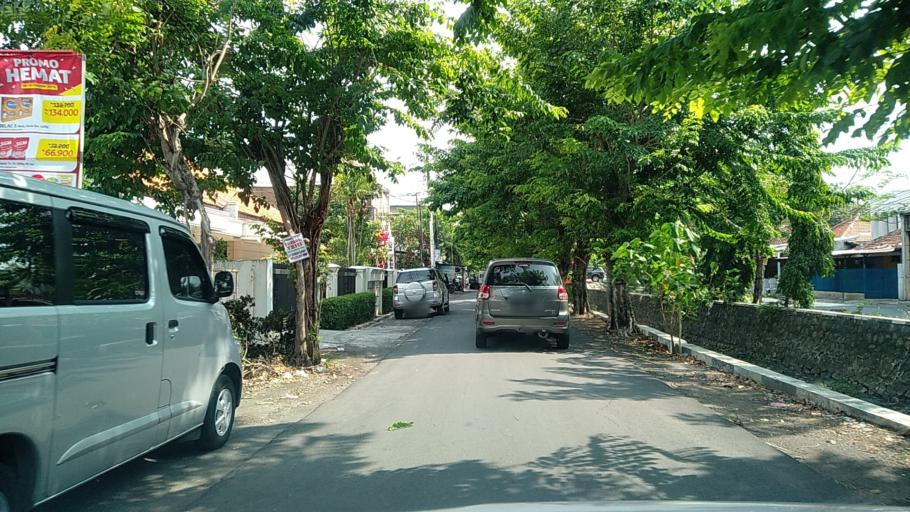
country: ID
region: Central Java
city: Semarang
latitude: -6.9873
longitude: 110.4372
